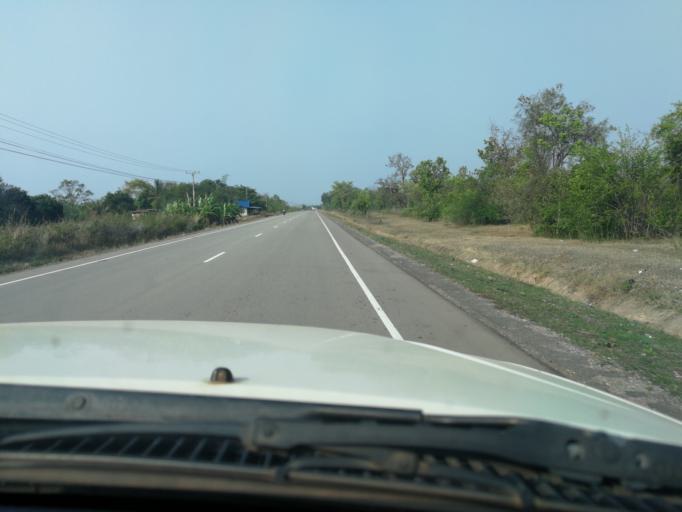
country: TH
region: Mukdahan
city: Wan Yai
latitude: 16.7088
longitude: 105.2398
